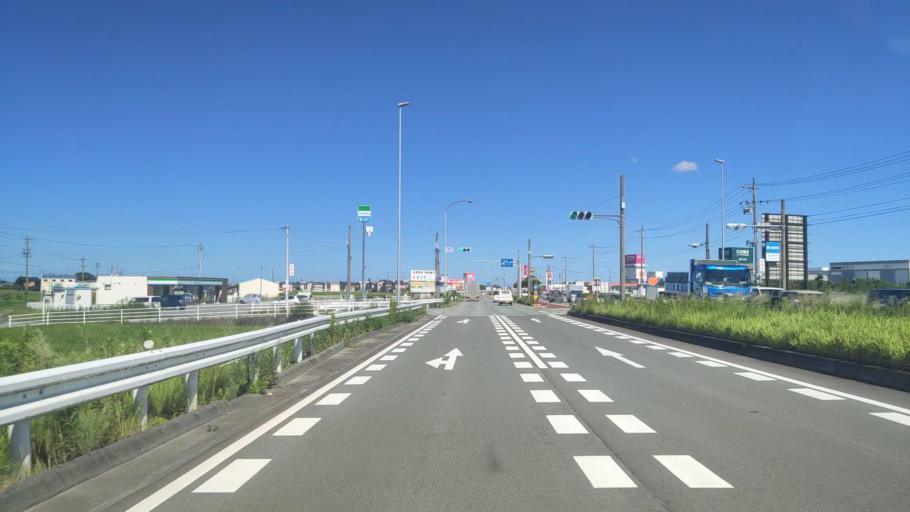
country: JP
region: Mie
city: Ise
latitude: 34.5845
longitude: 136.6099
